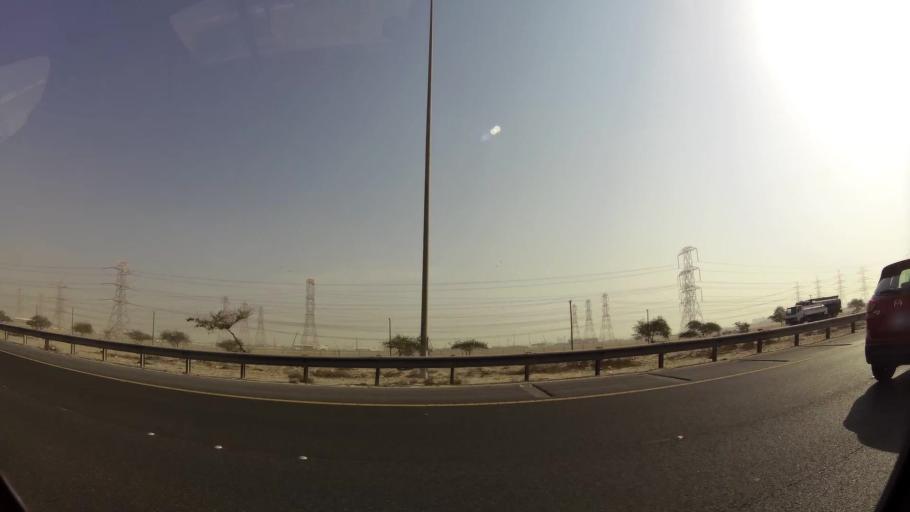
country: KW
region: Al Ahmadi
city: Al Ahmadi
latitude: 28.9967
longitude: 48.0987
